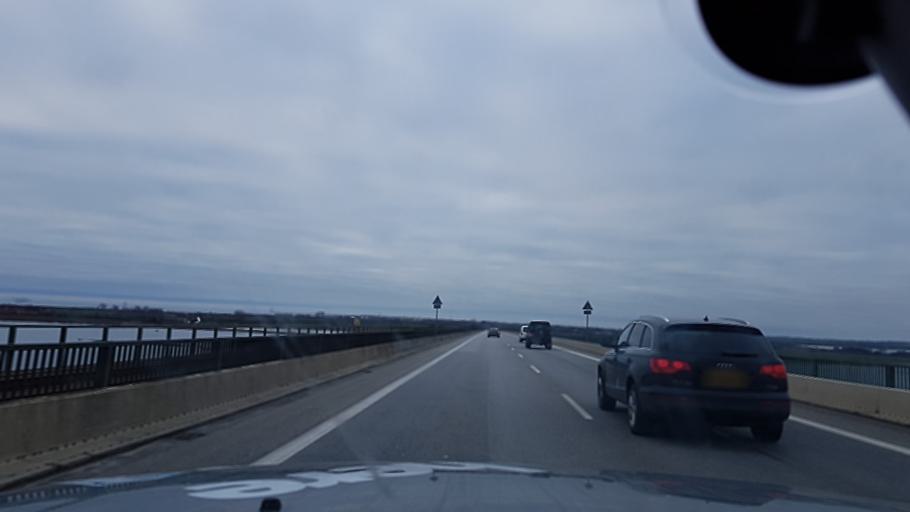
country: DE
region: Schleswig-Holstein
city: Grossenbrode
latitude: 54.4006
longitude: 11.1117
